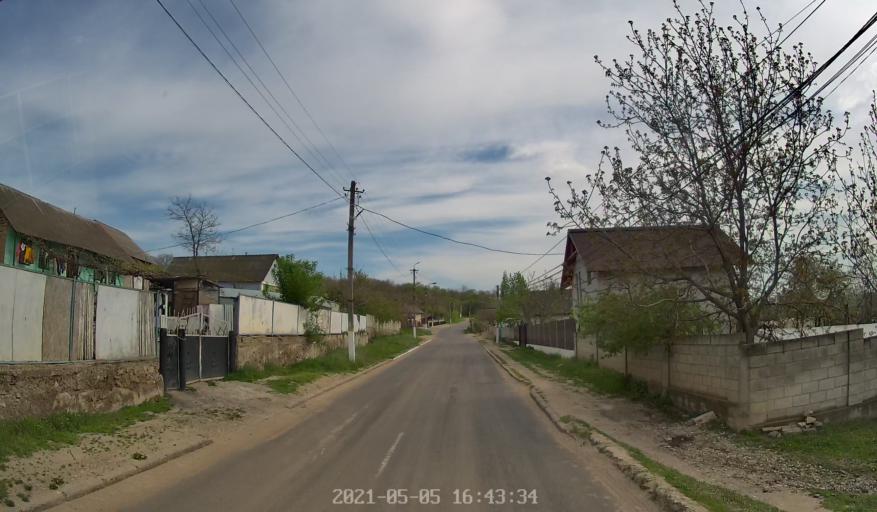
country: MD
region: Criuleni
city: Criuleni
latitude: 47.1228
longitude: 29.1940
